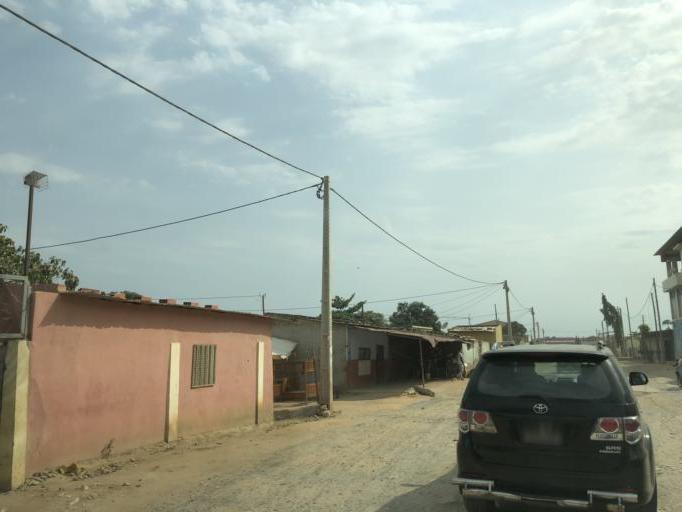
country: AO
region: Luanda
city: Luanda
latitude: -8.8989
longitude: 13.3500
